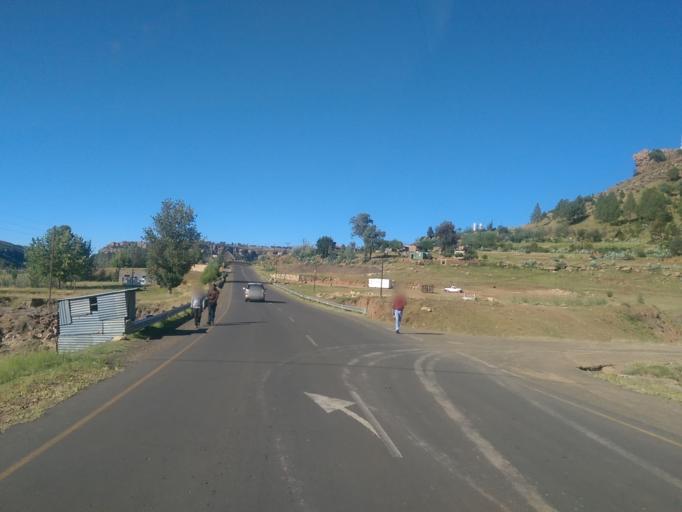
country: LS
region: Maseru
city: Maseru
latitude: -29.3491
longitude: 27.6616
